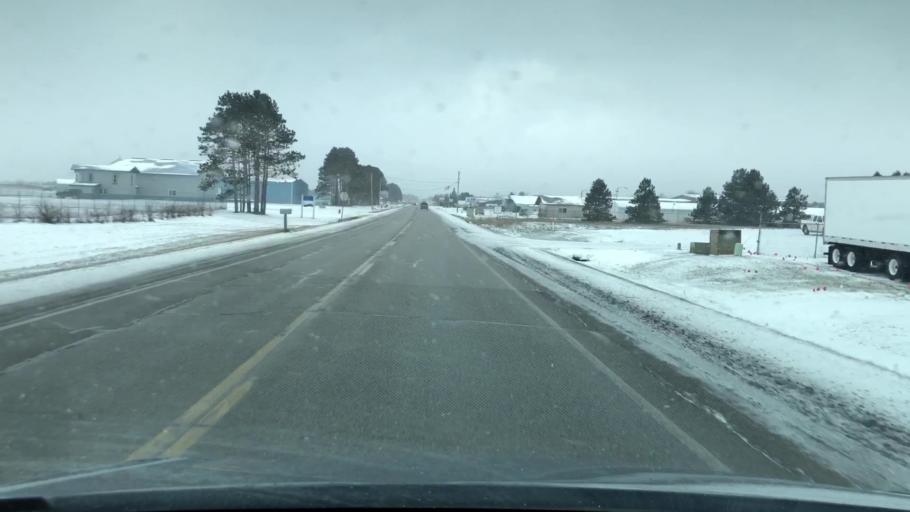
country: US
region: Michigan
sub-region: Wexford County
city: Cadillac
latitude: 44.2813
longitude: -85.4112
